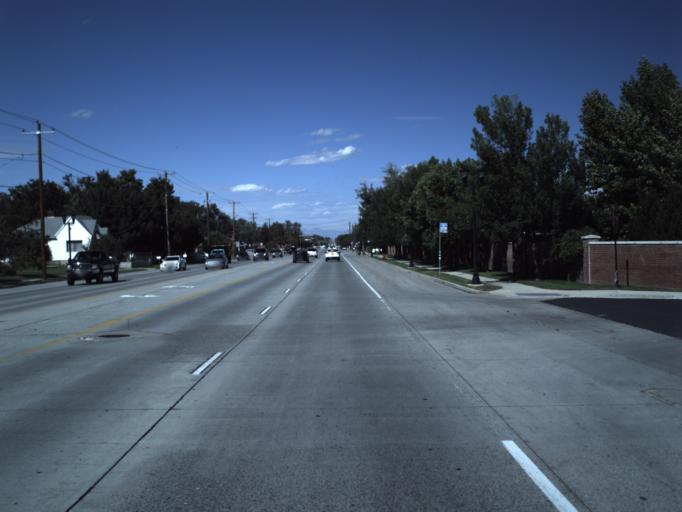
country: US
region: Utah
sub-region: Salt Lake County
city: South Jordan Heights
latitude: 40.5781
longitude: -111.9386
